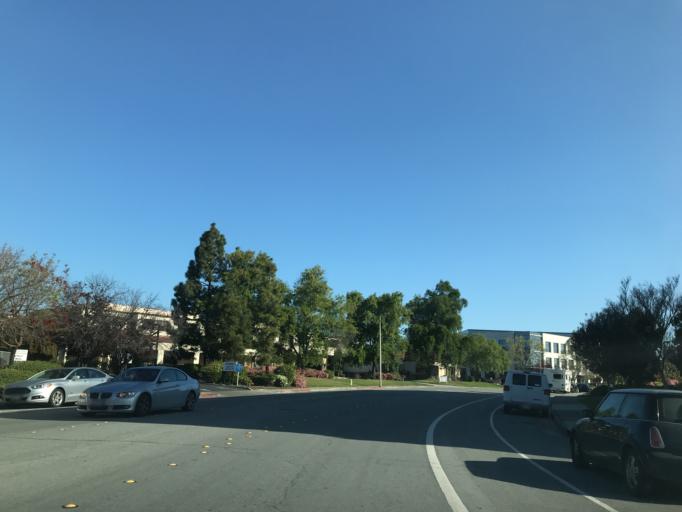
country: US
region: California
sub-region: San Mateo County
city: Redwood City
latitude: 37.4923
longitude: -122.2283
